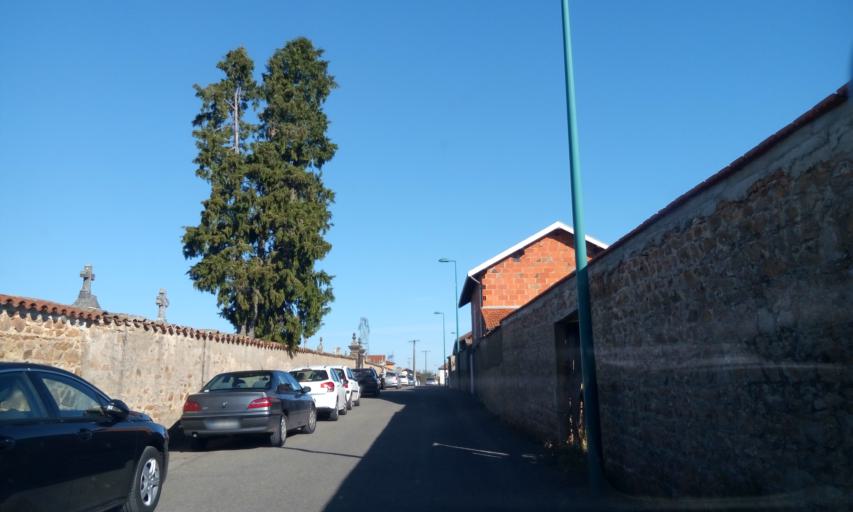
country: FR
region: Rhone-Alpes
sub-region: Departement de la Loire
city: Coutouvre
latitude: 46.0340
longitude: 4.2366
